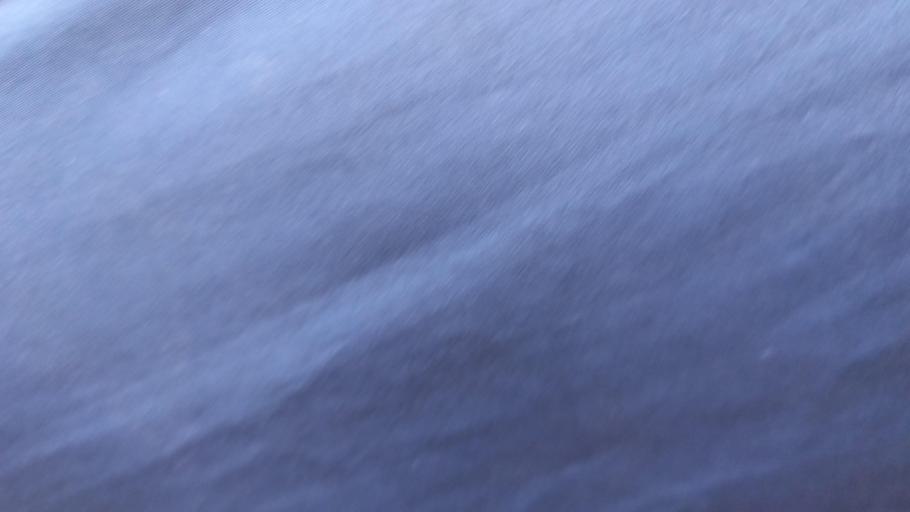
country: BD
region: Dhaka
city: Azimpur
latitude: 23.6644
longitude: 90.3306
